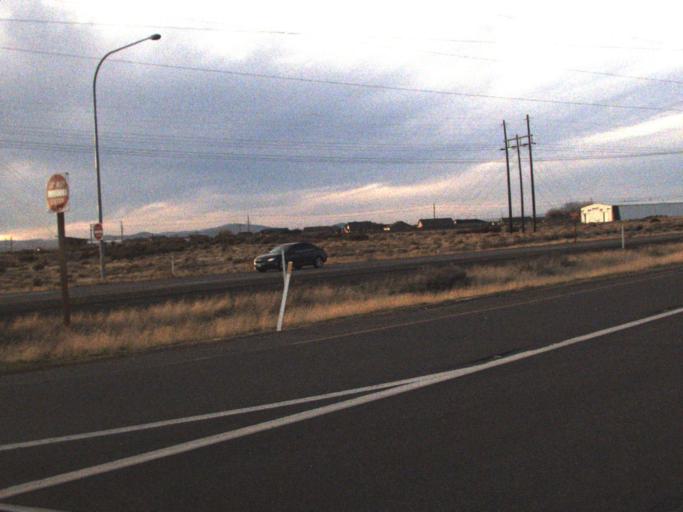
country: US
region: Washington
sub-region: Walla Walla County
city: Burbank
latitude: 46.2273
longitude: -119.0389
